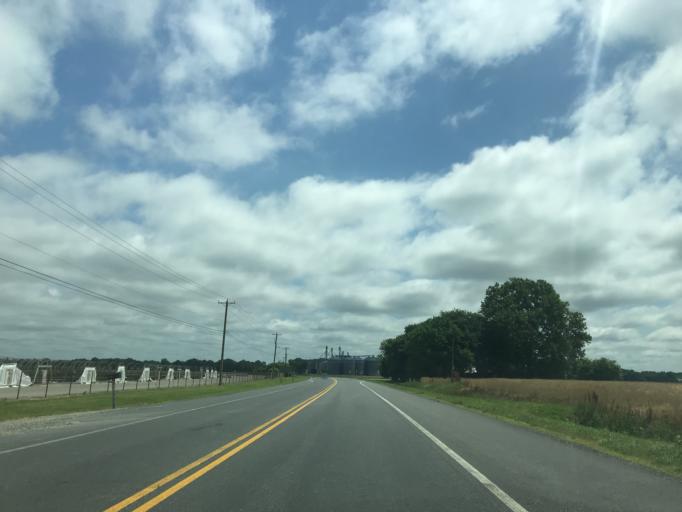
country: US
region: Maryland
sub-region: Caroline County
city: Ridgely
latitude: 38.9343
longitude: -75.8969
